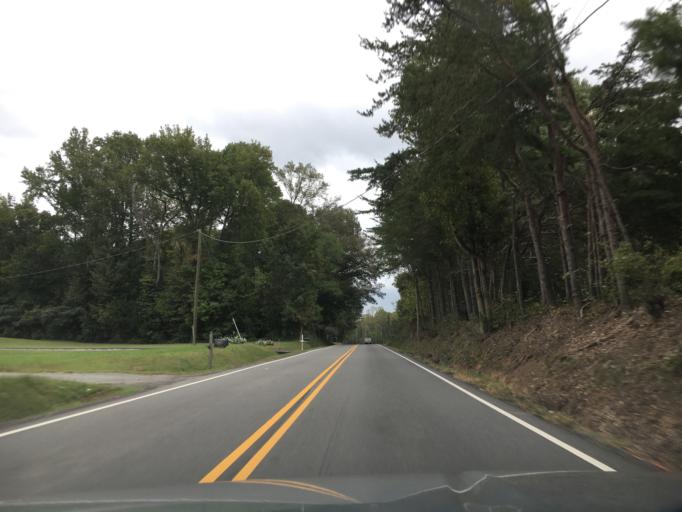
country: US
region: Virginia
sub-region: Goochland County
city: Goochland
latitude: 37.6985
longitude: -77.8538
